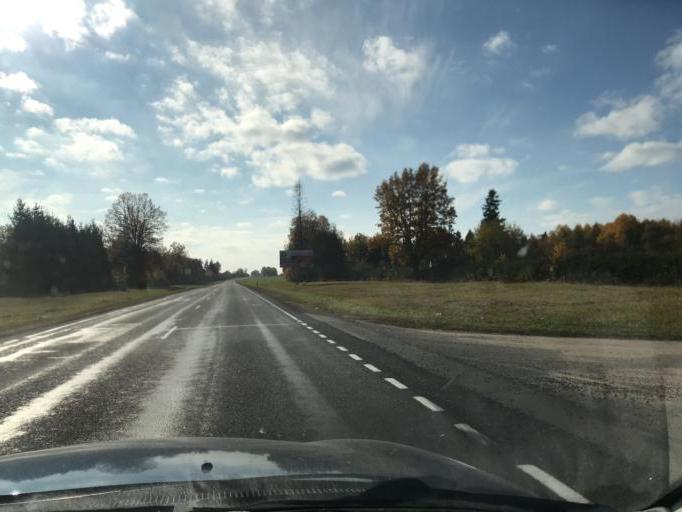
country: BY
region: Grodnenskaya
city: Voranava
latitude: 54.1772
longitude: 25.3342
